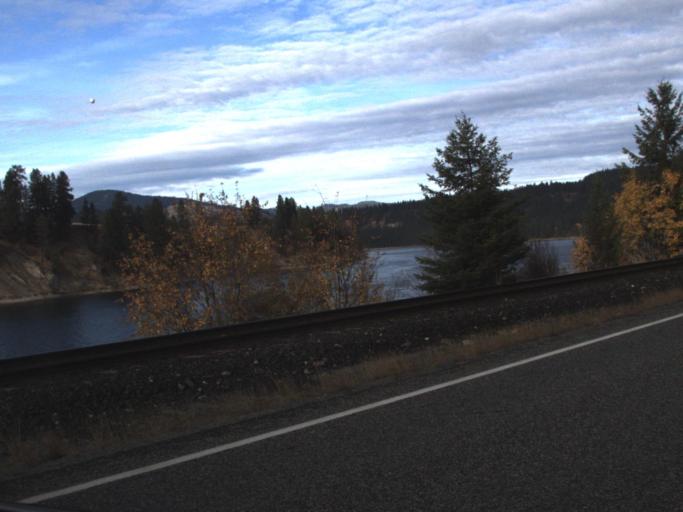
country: US
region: Washington
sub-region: Stevens County
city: Kettle Falls
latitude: 48.7719
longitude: -118.0176
